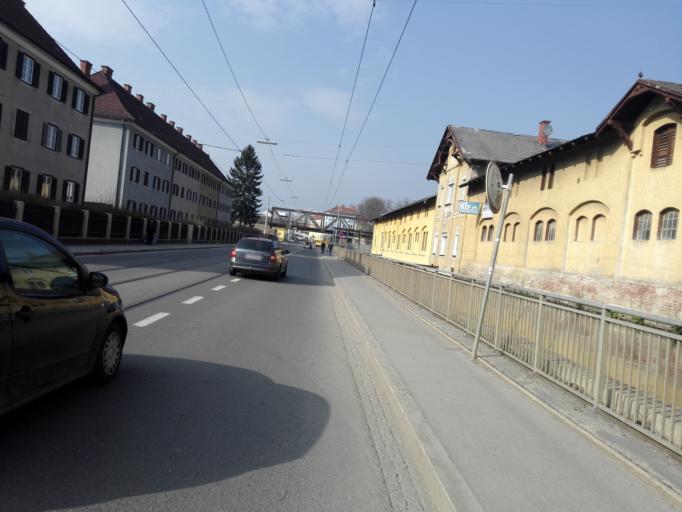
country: AT
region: Styria
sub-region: Graz Stadt
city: Graz
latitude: 47.0550
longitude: 15.4320
